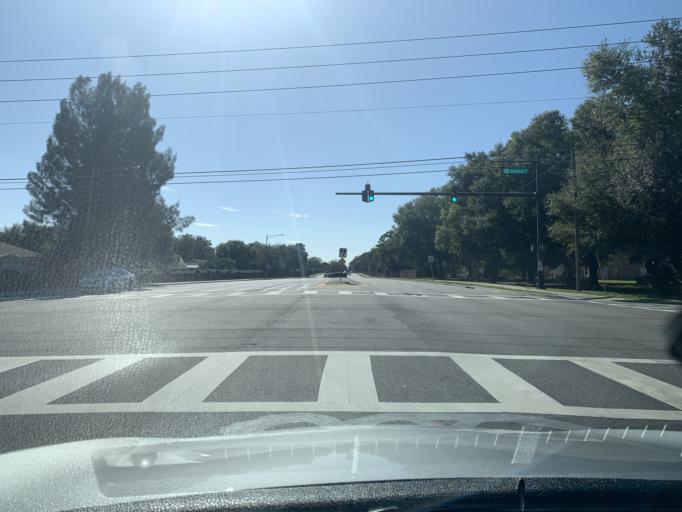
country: US
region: Florida
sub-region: Orange County
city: Clarcona
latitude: 28.6258
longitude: -81.4764
